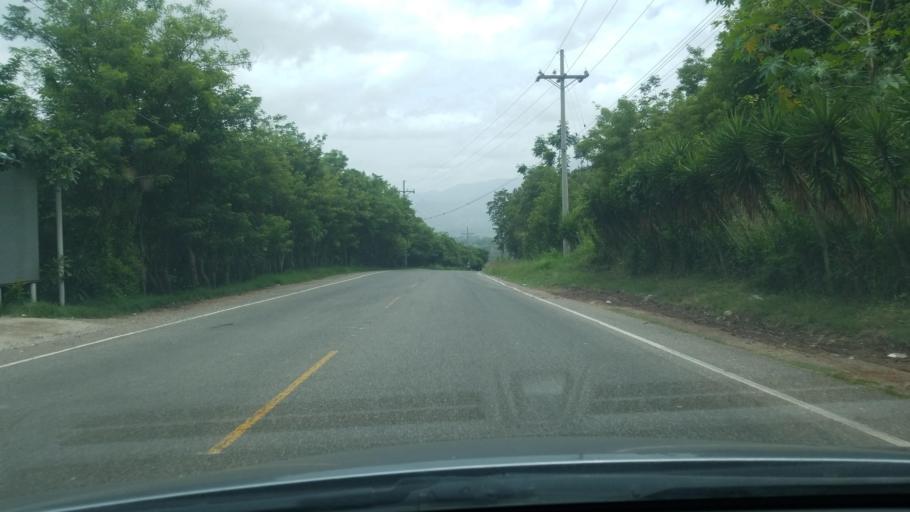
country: HN
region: Copan
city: Ojos de Agua
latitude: 14.6748
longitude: -88.8223
